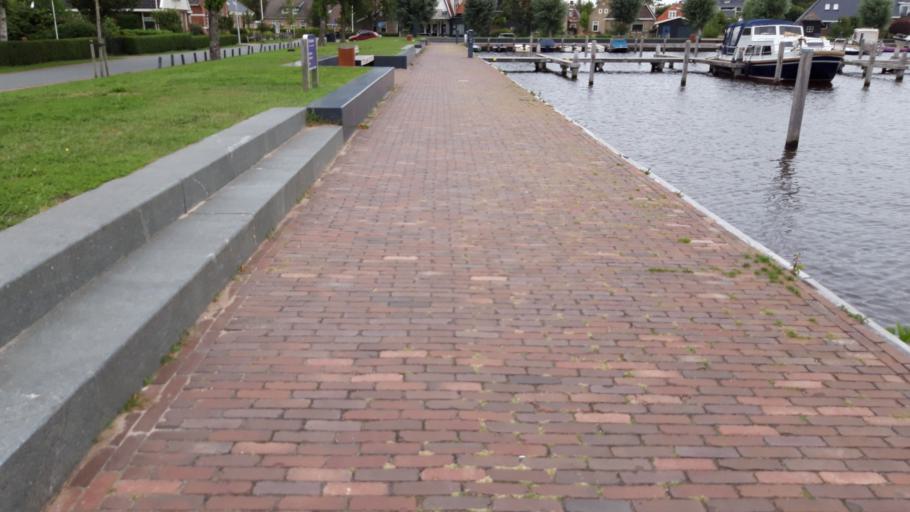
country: NL
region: Friesland
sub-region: Gemeente Boarnsterhim
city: Warten
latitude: 53.1305
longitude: 5.9403
